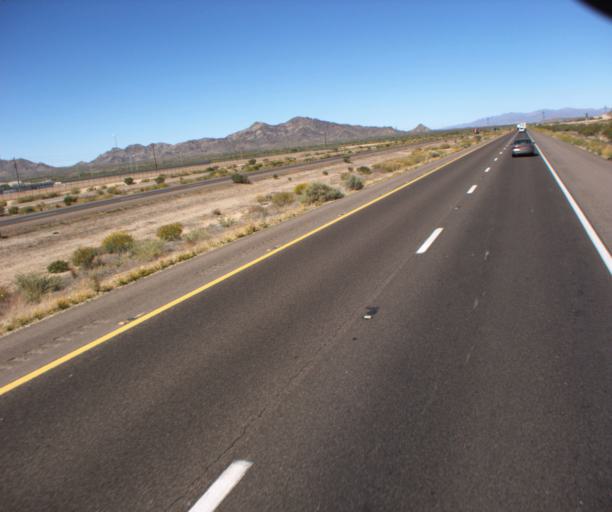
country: US
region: Arizona
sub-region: Maricopa County
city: Buckeye
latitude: 33.2111
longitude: -112.6455
